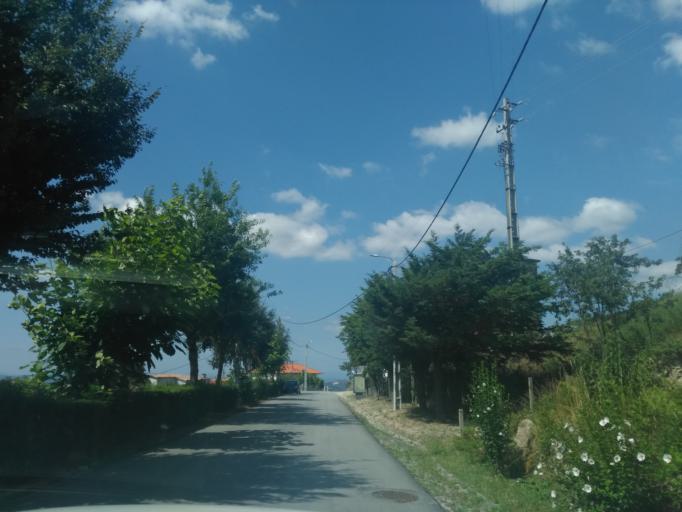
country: PT
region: Porto
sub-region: Baiao
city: Baiao
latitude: 41.2354
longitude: -7.9989
